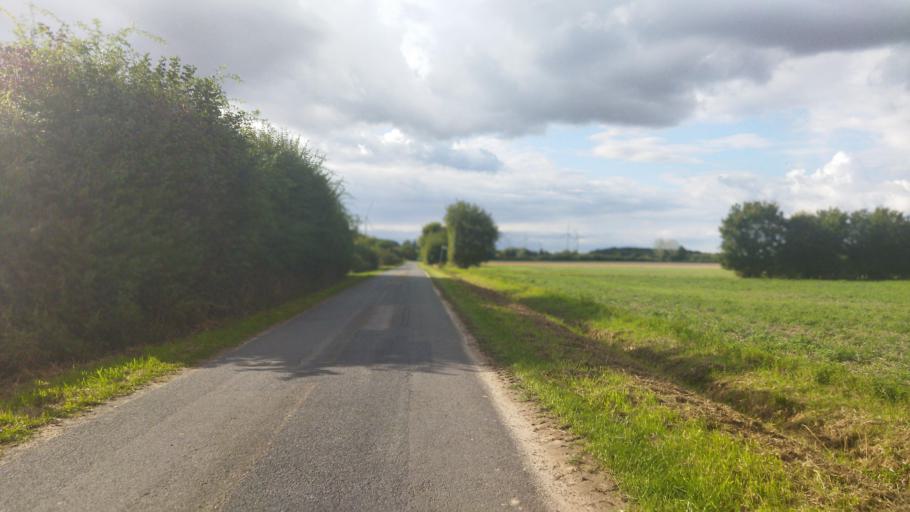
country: DE
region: North Rhine-Westphalia
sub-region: Regierungsbezirk Munster
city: Dulmen
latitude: 51.8783
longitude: 7.2574
